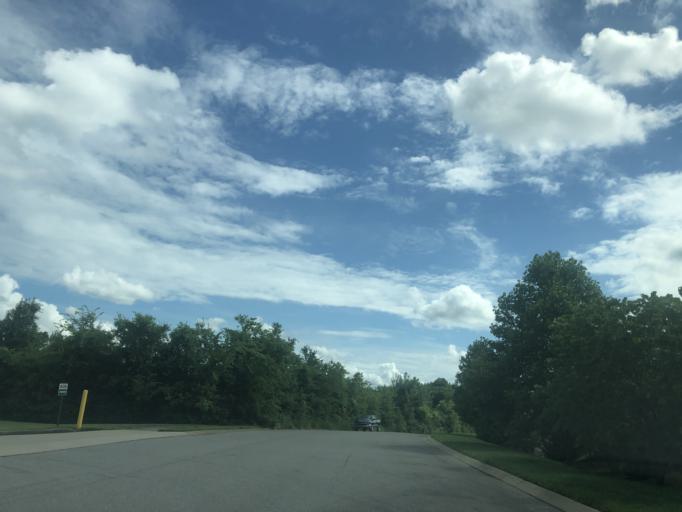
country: US
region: Tennessee
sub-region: Davidson County
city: Nashville
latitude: 36.2074
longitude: -86.8680
